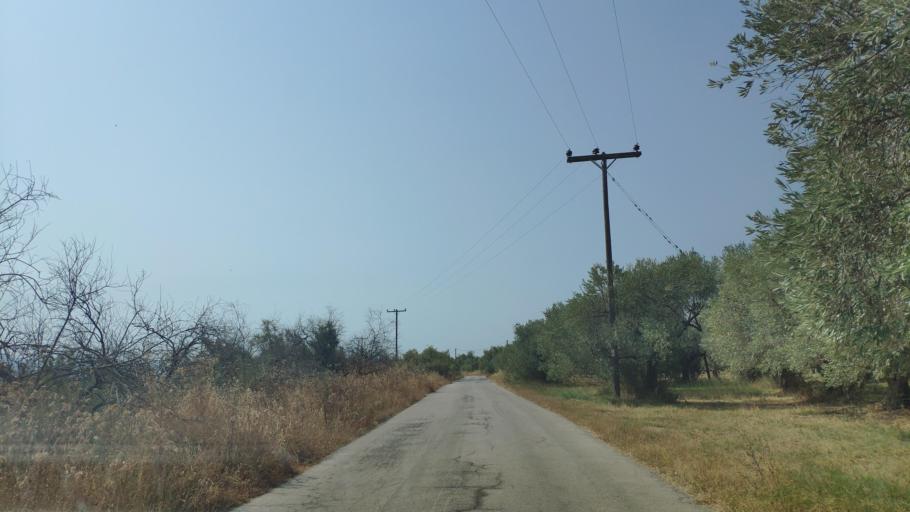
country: GR
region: West Greece
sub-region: Nomos Aitolias kai Akarnanias
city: Menidi
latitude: 39.0443
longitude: 21.0723
